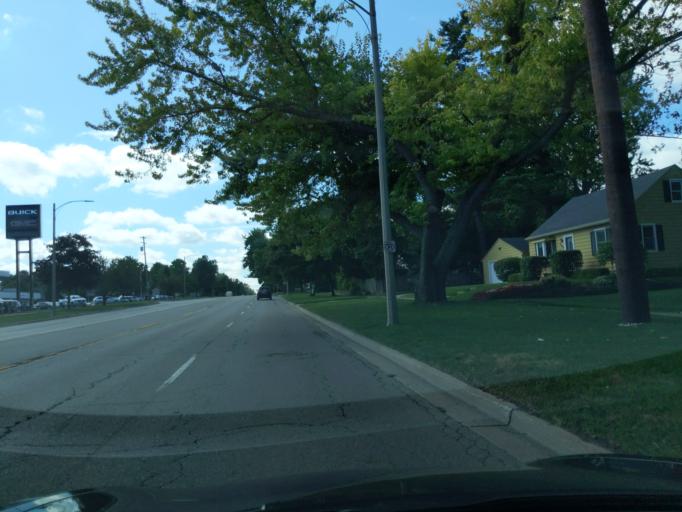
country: US
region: Michigan
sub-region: Ingham County
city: Lansing
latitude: 42.6956
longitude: -84.5382
